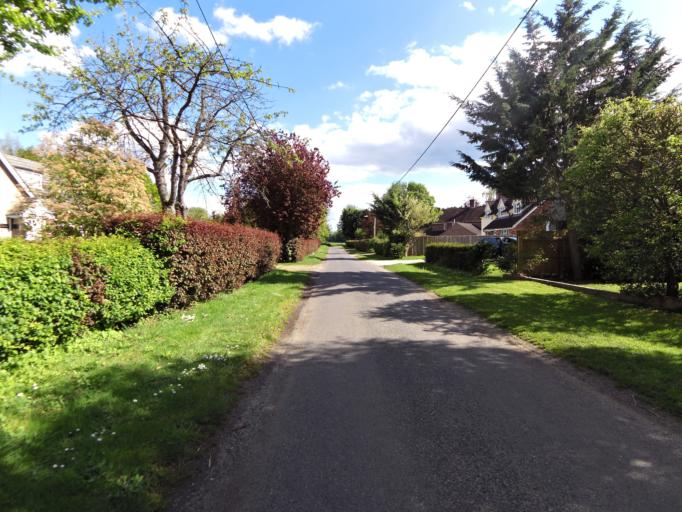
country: GB
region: England
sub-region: Suffolk
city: Thurston
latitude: 52.2425
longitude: 0.8273
